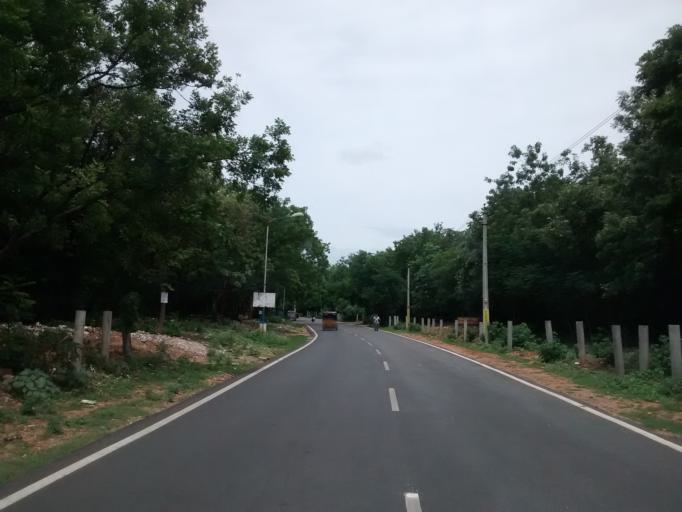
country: IN
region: Andhra Pradesh
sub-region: Chittoor
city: Akkarampalle
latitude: 13.6454
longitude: 79.4030
